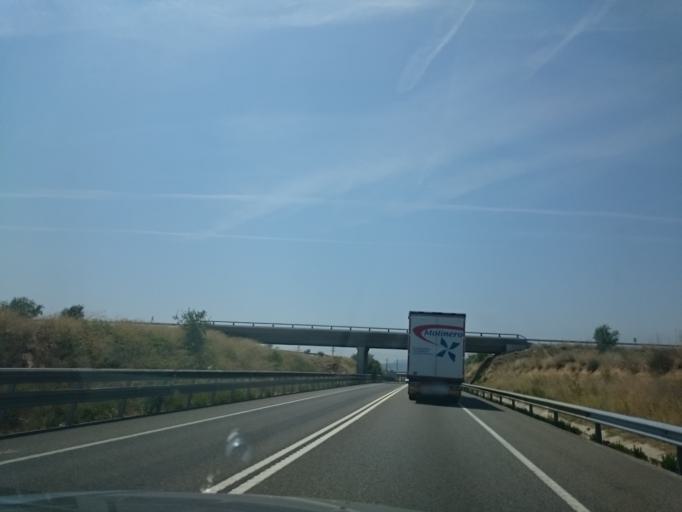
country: ES
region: Catalonia
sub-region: Provincia de Barcelona
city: Vilafranca del Penedes
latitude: 41.3341
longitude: 1.6985
